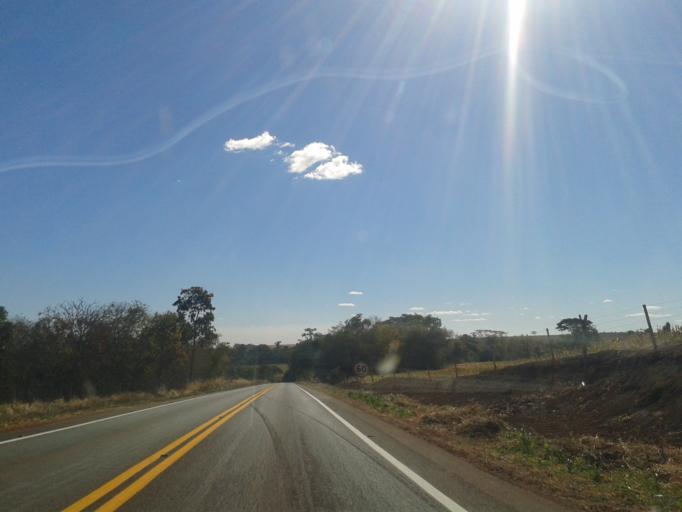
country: BR
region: Minas Gerais
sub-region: Capinopolis
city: Capinopolis
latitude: -18.6784
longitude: -49.5571
